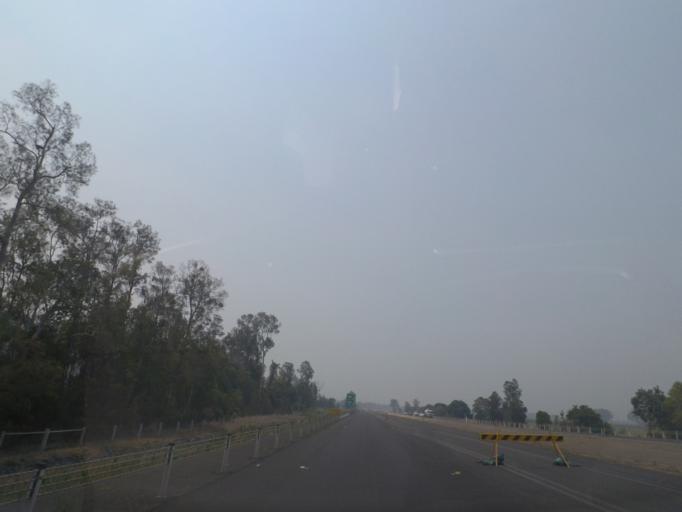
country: AU
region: New South Wales
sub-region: Ballina
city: Ballina
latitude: -28.8774
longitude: 153.4880
